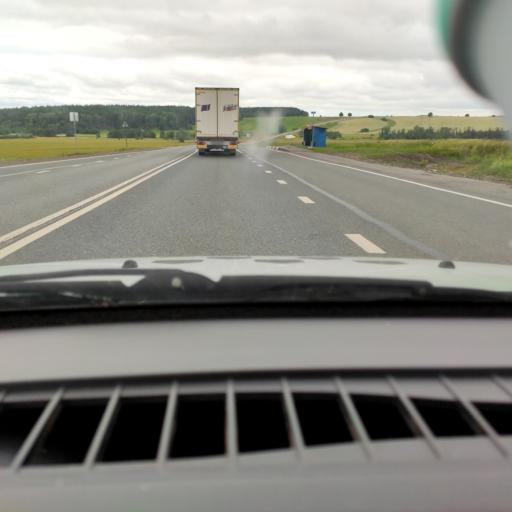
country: RU
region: Udmurtiya
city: Alnashi
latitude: 56.1187
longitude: 52.4616
